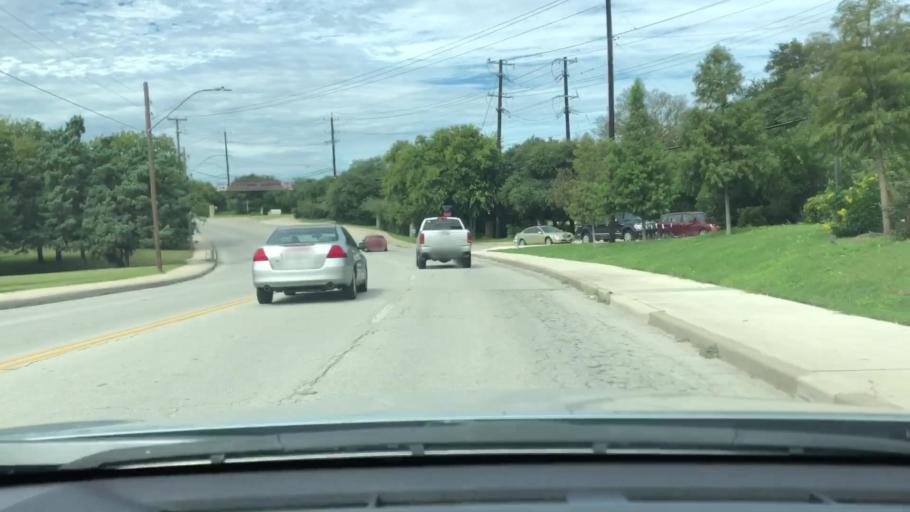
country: US
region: Texas
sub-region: Bexar County
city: Olmos Park
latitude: 29.4662
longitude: -98.4810
